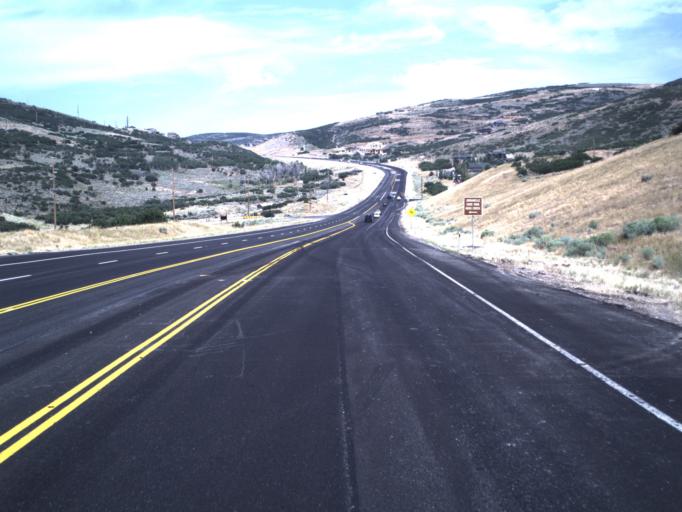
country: US
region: Utah
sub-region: Summit County
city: Park City
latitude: 40.6575
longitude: -111.4134
